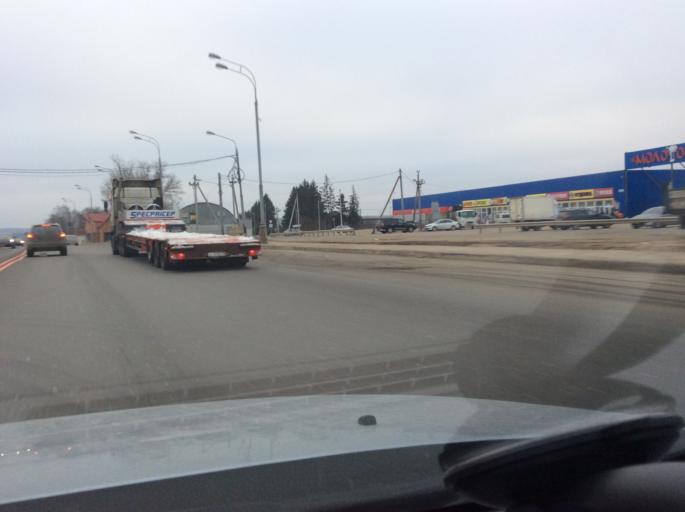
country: RU
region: Moskovskaya
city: Troitsk
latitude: 55.4508
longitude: 37.2911
